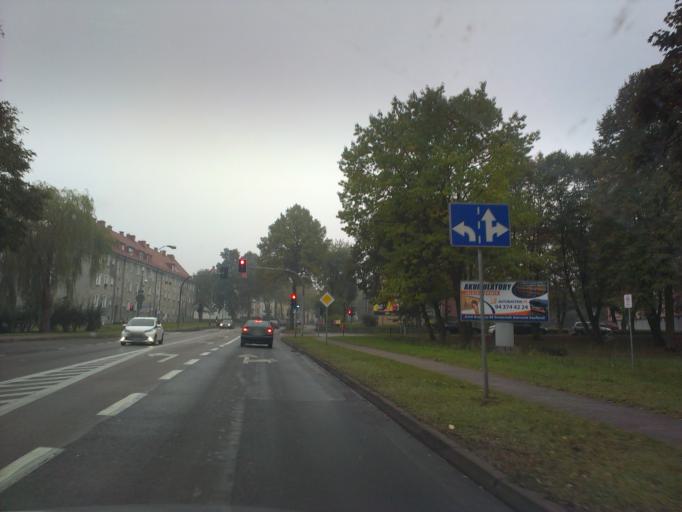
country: PL
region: West Pomeranian Voivodeship
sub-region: Powiat szczecinecki
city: Szczecinek
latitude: 53.7069
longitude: 16.7096
